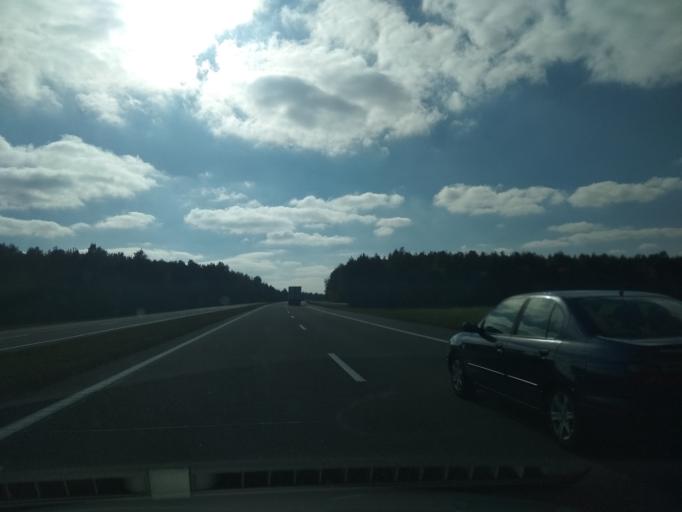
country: BY
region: Brest
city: Baranovichi
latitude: 53.0774
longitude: 25.8846
